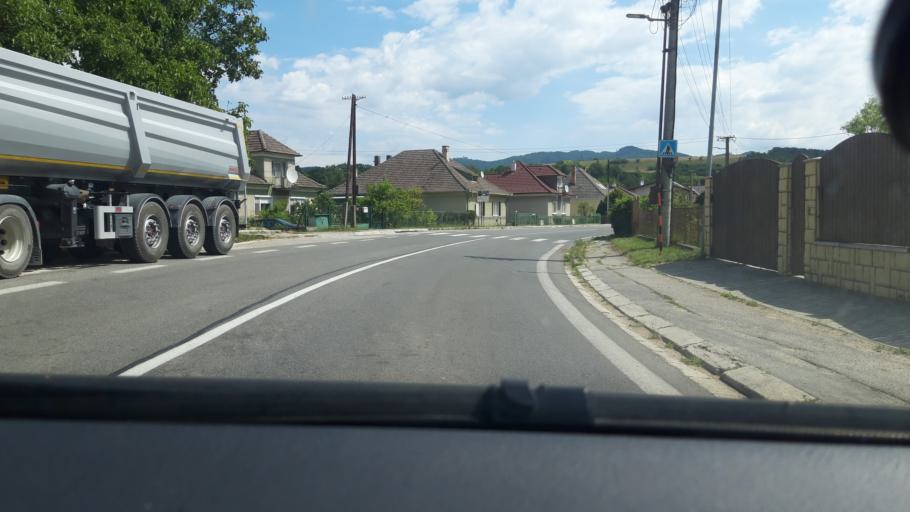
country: SK
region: Trnavsky
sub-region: Okres Trnava
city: Piestany
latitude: 48.6476
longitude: 17.8769
